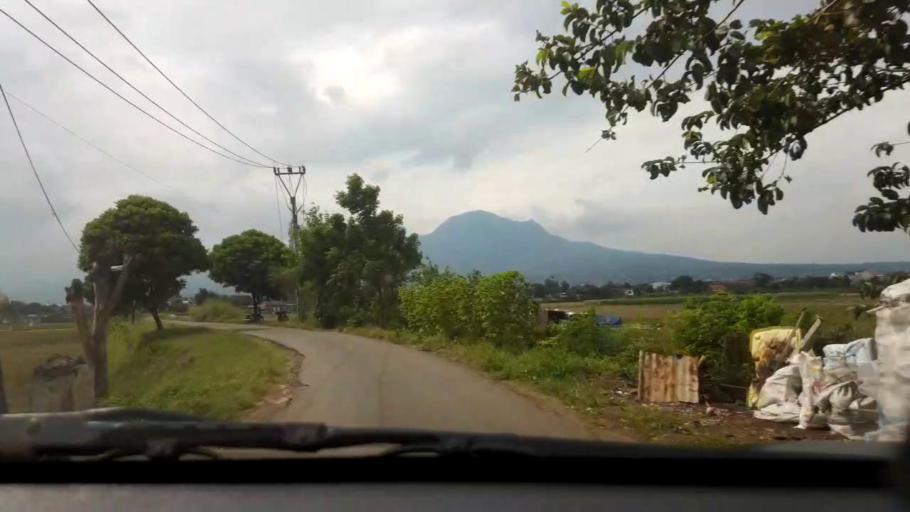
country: ID
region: West Java
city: Cileunyi
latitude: -6.9527
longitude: 107.7130
